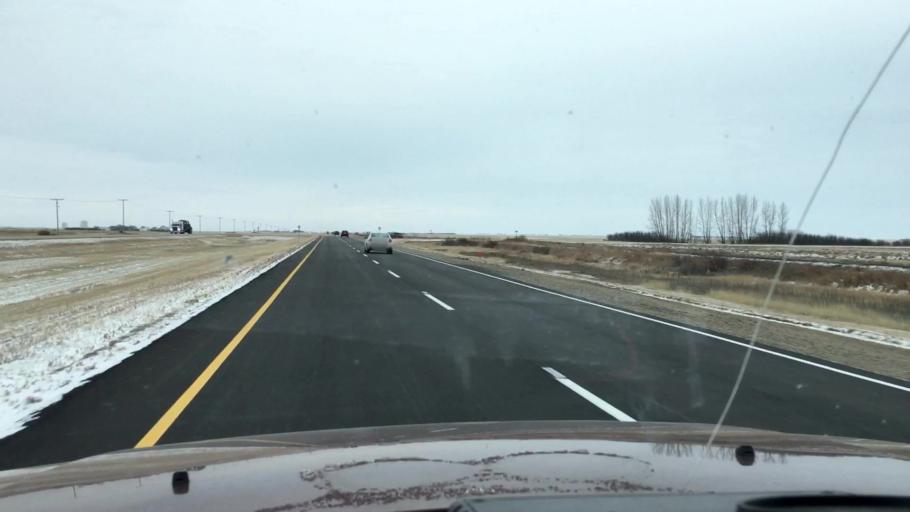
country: CA
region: Saskatchewan
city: Watrous
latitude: 51.1415
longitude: -105.9039
